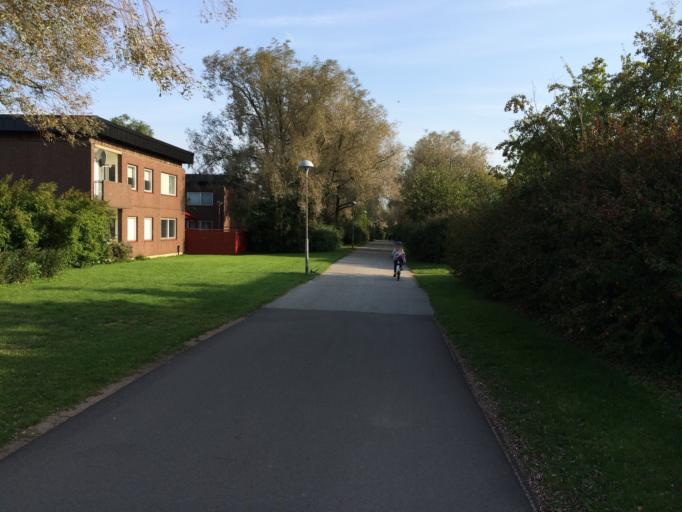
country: SE
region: Skane
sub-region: Lunds Kommun
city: Lund
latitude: 55.7108
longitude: 13.2333
